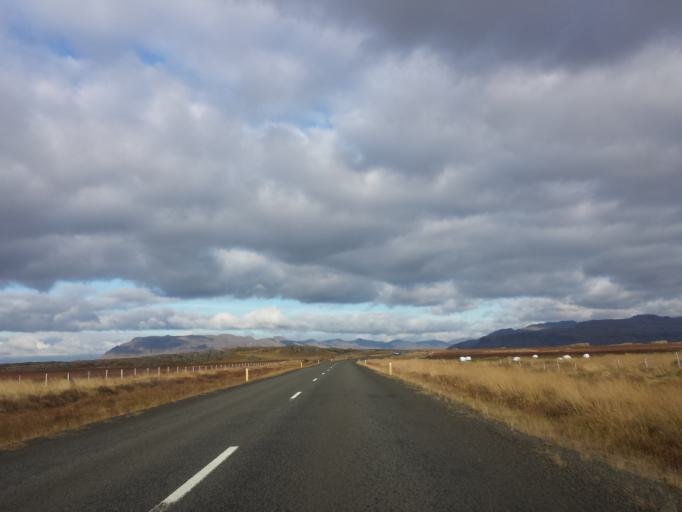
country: IS
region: West
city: Borgarnes
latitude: 64.6682
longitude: -22.0704
